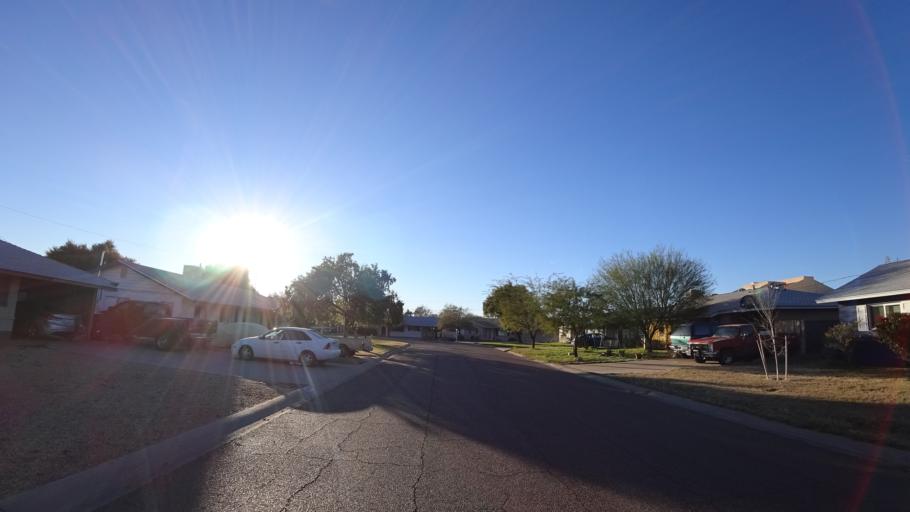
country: US
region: Arizona
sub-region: Maricopa County
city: Phoenix
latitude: 33.4868
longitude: -112.0374
